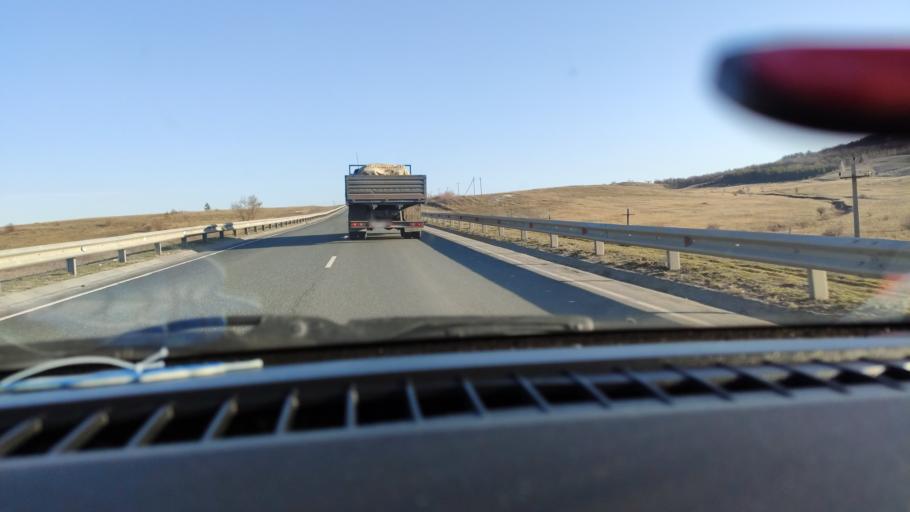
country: RU
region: Saratov
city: Alekseyevka
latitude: 52.3156
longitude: 47.9232
